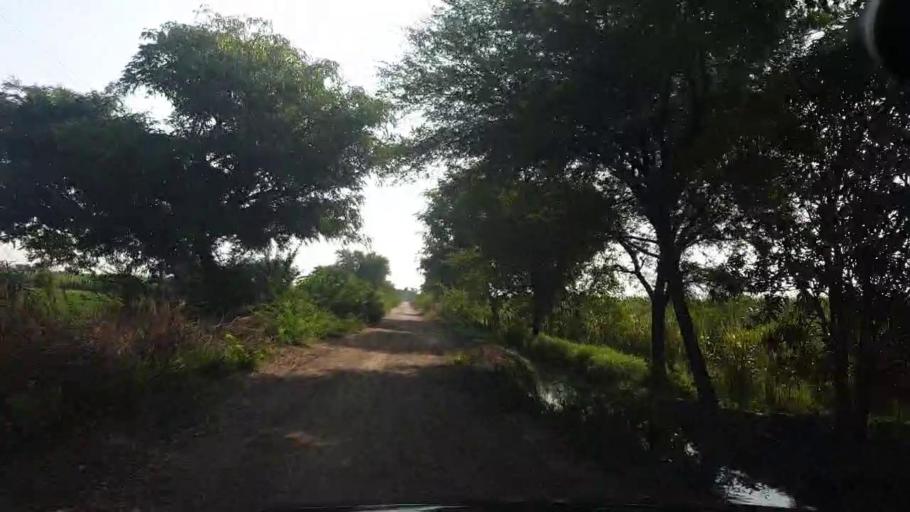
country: PK
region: Sindh
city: Tando Bago
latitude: 24.6509
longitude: 69.1699
